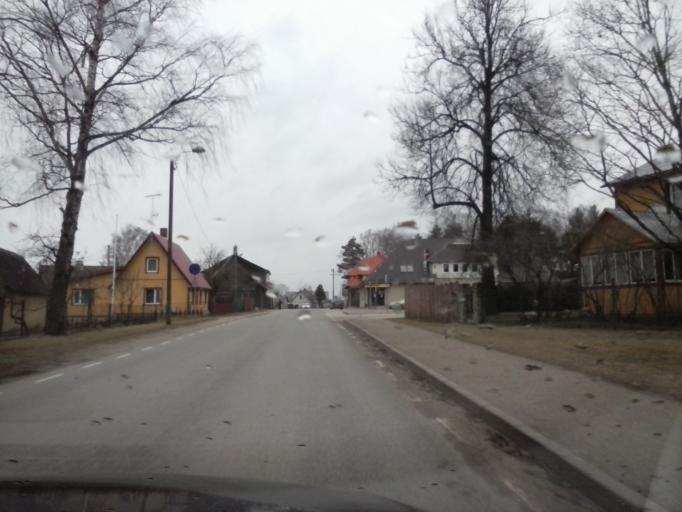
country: RU
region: Pskov
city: Pechory
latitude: 57.9584
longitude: 27.6319
